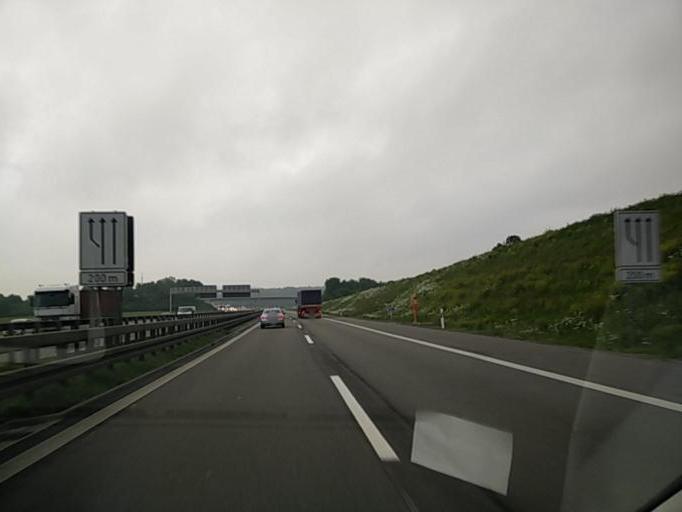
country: DE
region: Baden-Wuerttemberg
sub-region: Regierungsbezirk Stuttgart
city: Ehningen
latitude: 48.6387
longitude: 8.9265
